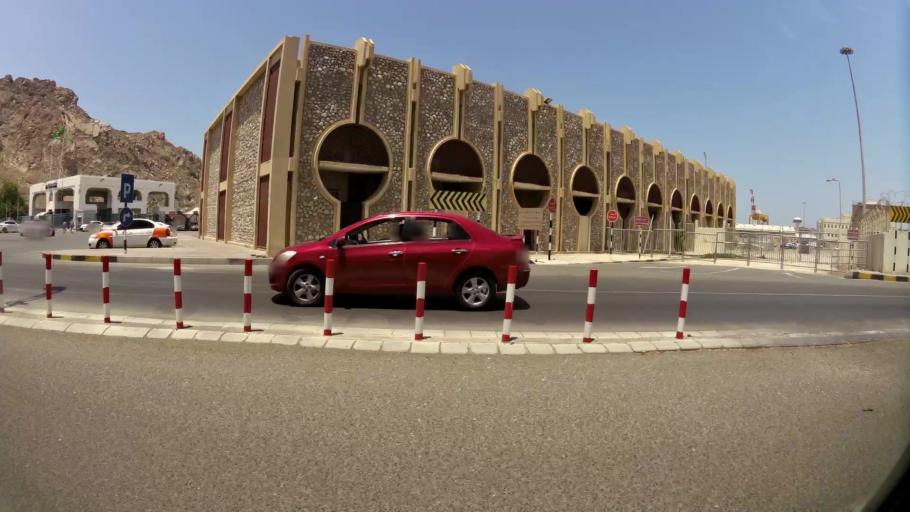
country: OM
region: Muhafazat Masqat
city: Muscat
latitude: 23.6262
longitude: 58.5619
